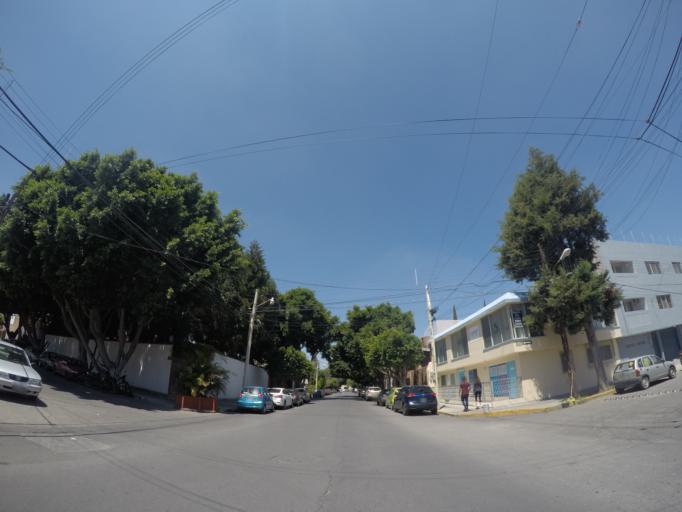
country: MX
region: San Luis Potosi
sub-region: San Luis Potosi
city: San Luis Potosi
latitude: 22.1477
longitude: -101.0045
